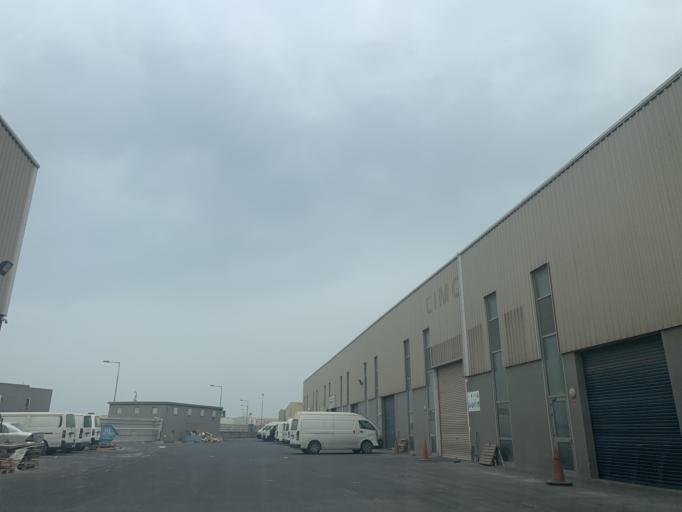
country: BH
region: Muharraq
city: Al Hadd
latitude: 26.2126
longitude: 50.6696
